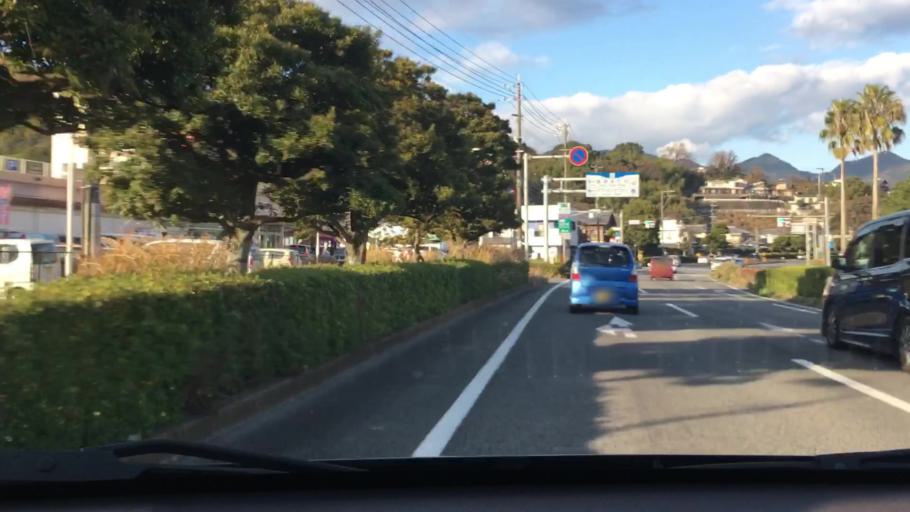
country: JP
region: Oita
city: Hiji
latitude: 33.3432
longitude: 131.4944
